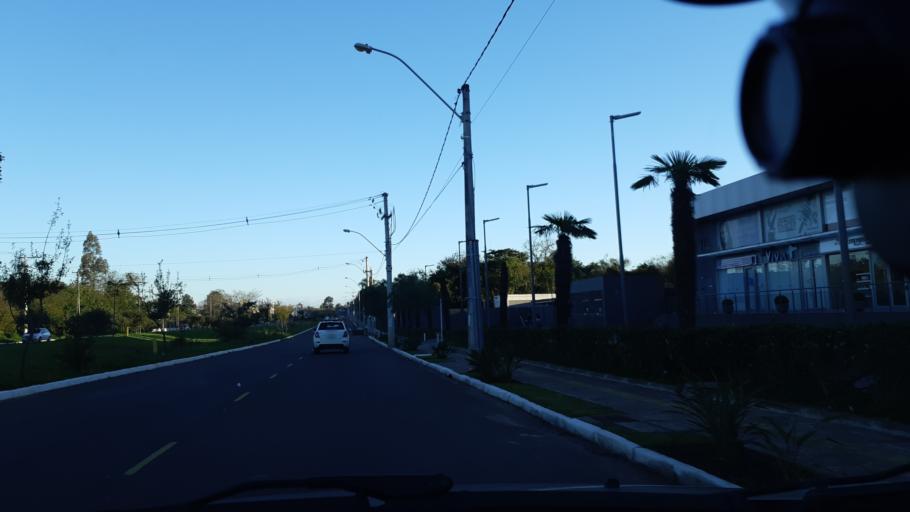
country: BR
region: Rio Grande do Sul
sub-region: Canoas
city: Canoas
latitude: -29.9190
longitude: -51.1552
